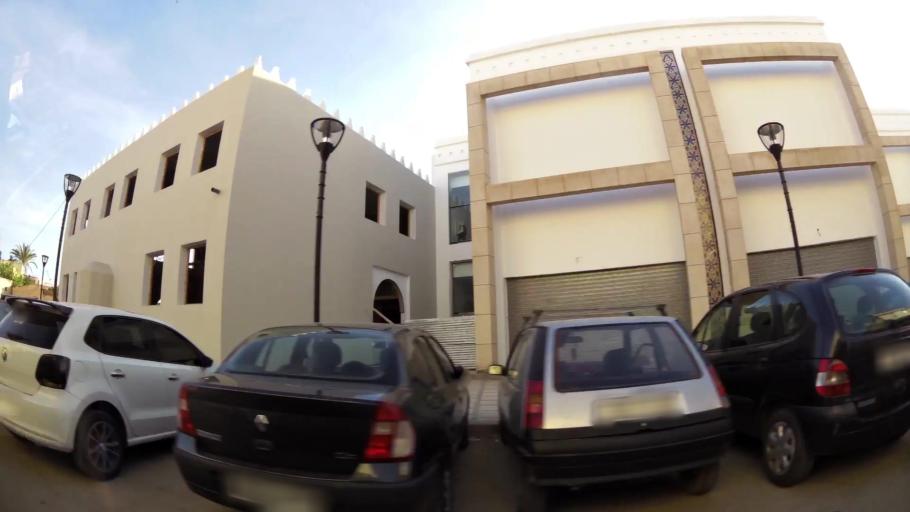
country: MA
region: Oriental
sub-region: Oujda-Angad
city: Oujda
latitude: 34.6786
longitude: -1.9054
